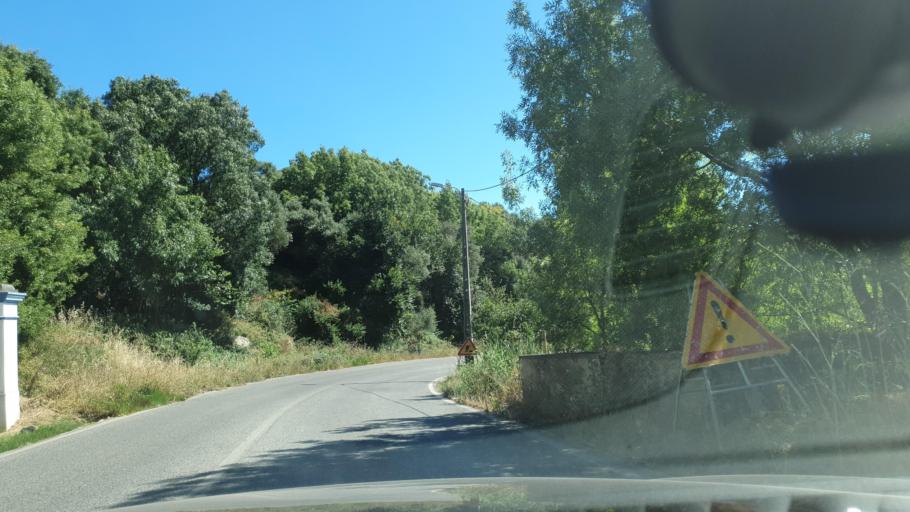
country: PT
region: Lisbon
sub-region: Sintra
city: Belas
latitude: 38.7809
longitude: -9.2595
